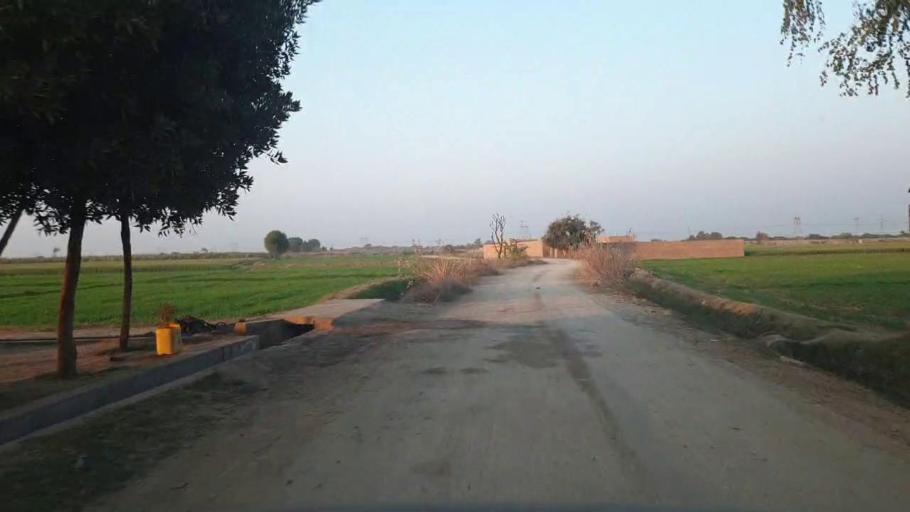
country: PK
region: Sindh
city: Bhit Shah
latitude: 25.8135
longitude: 68.5020
